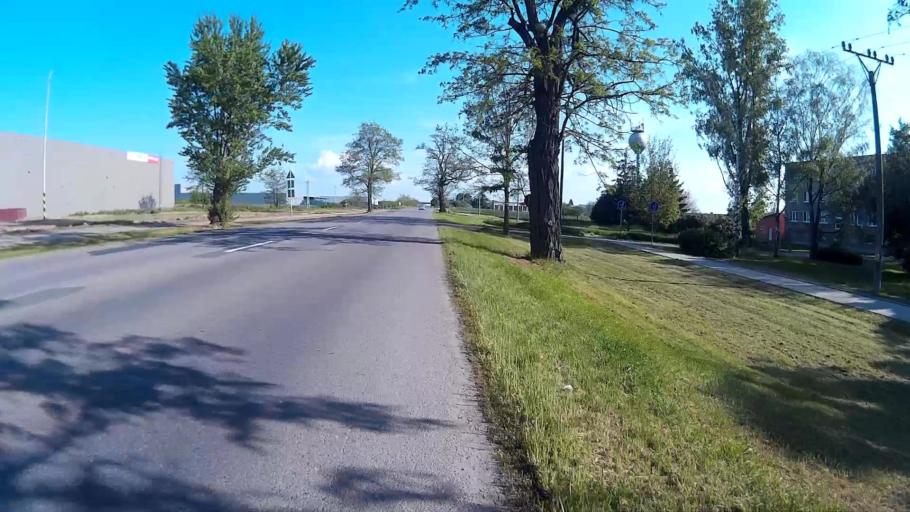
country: CZ
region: South Moravian
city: Pohorelice
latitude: 48.9754
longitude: 16.5157
